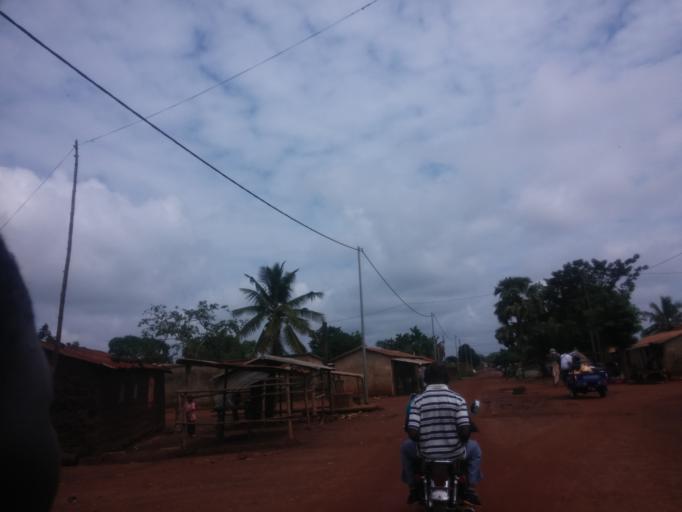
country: TG
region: Centrale
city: Sotouboua
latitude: 8.5558
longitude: 0.9837
